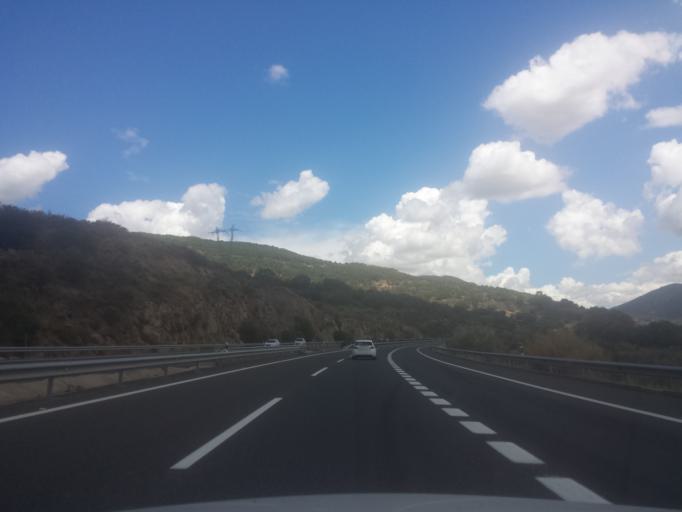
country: ES
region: Extremadura
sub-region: Provincia de Caceres
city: Hervas
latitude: 40.2900
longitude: -5.8991
